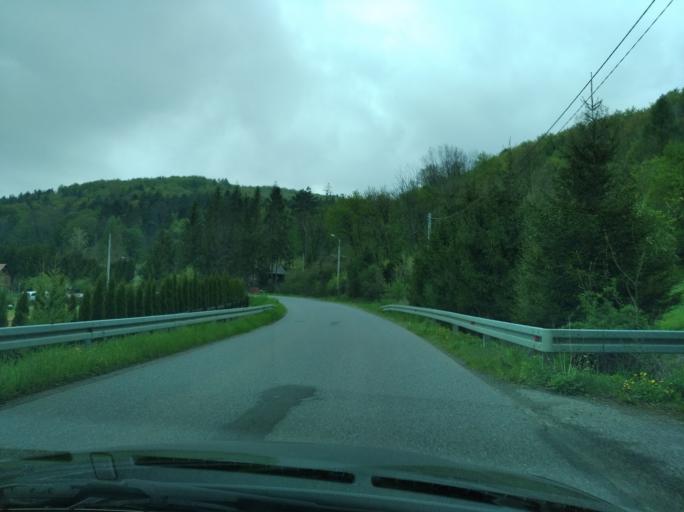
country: PL
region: Subcarpathian Voivodeship
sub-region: Powiat sanocki
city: Sanok
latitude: 49.6052
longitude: 22.2097
